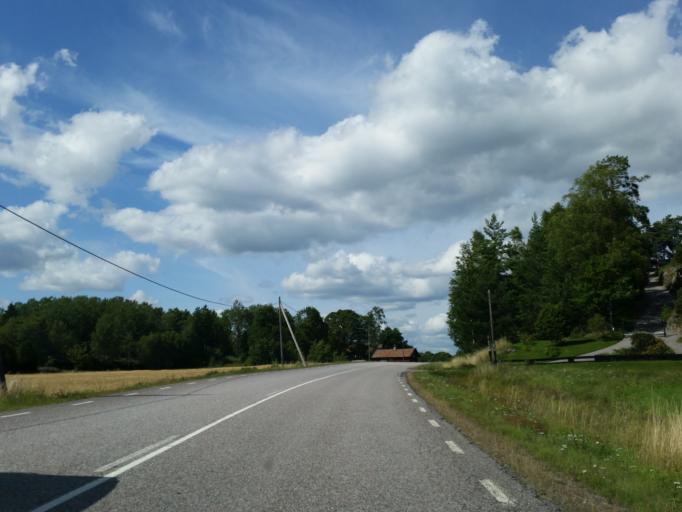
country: SE
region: Soedermanland
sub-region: Trosa Kommun
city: Vagnharad
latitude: 58.9998
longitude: 17.6054
